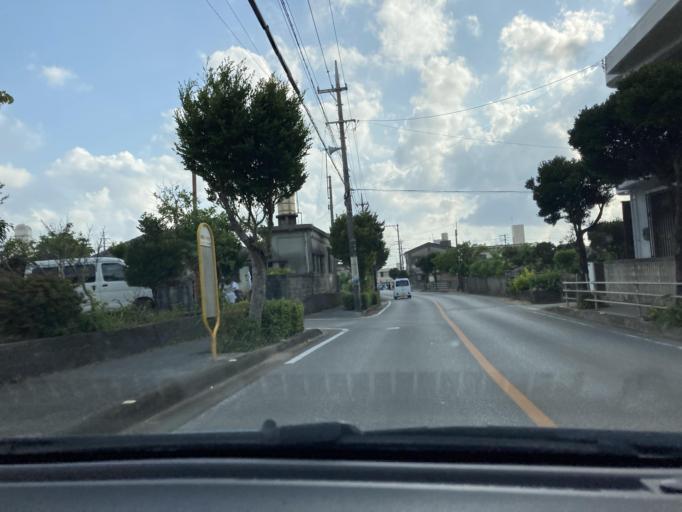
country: JP
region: Okinawa
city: Itoman
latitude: 26.0937
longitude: 127.6642
